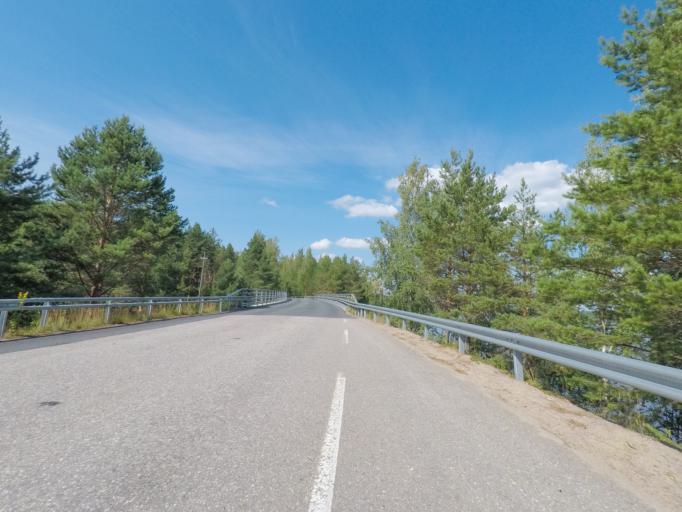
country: FI
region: Southern Savonia
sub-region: Mikkeli
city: Puumala
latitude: 61.4682
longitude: 28.1692
